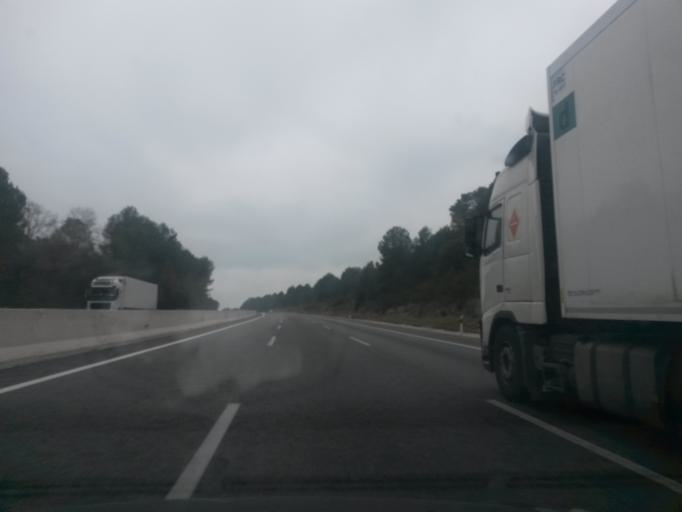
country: ES
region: Catalonia
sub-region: Provincia de Girona
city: Cervia de Ter
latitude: 42.0966
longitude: 2.8970
